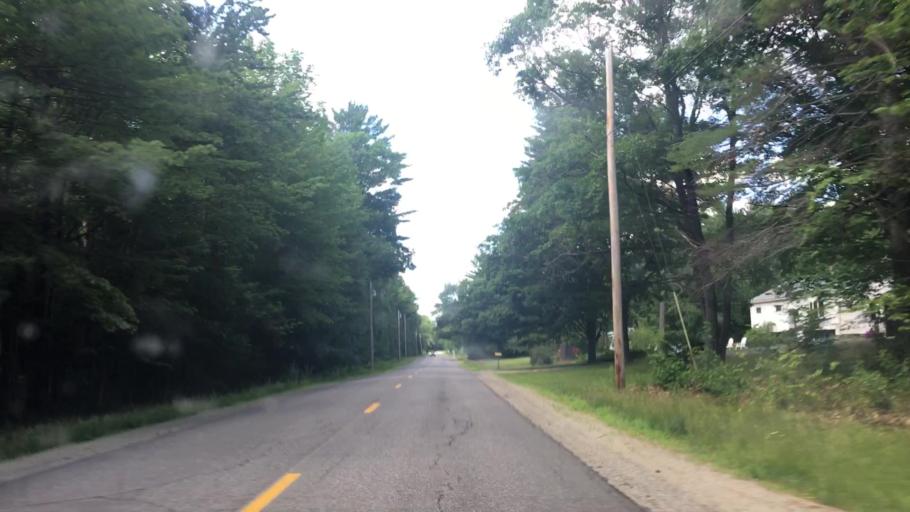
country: US
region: Maine
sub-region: Franklin County
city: Chesterville
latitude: 44.6049
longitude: -70.0836
